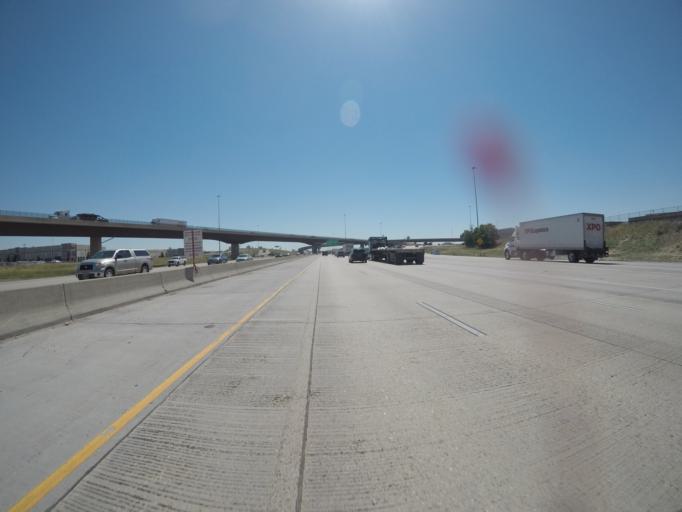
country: US
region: Colorado
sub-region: Adams County
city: Aurora
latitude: 39.7728
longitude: -104.8326
